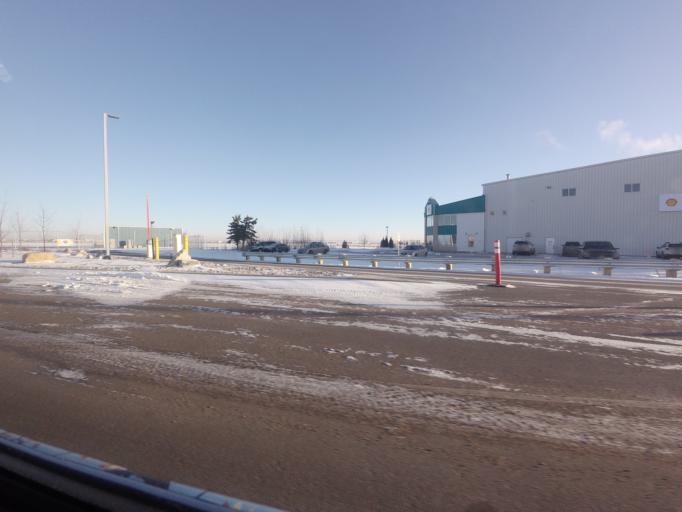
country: CA
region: Saskatchewan
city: Saskatoon
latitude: 52.1701
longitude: -106.6870
